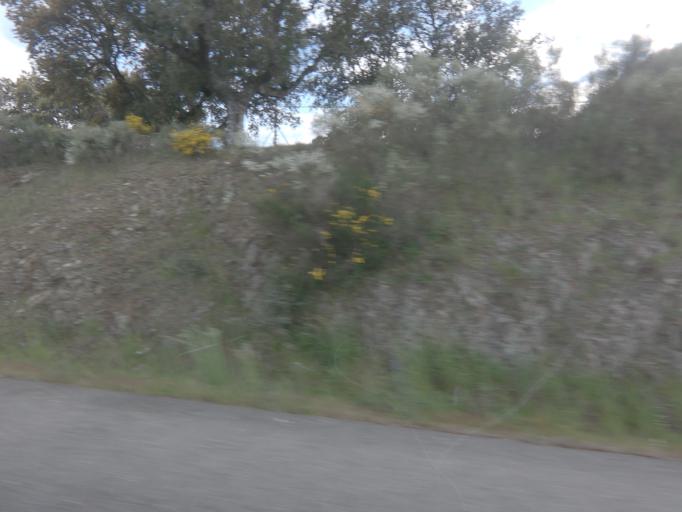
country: ES
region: Extremadura
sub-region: Provincia de Caceres
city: Pedroso de Acim
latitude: 39.8310
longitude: -6.3829
